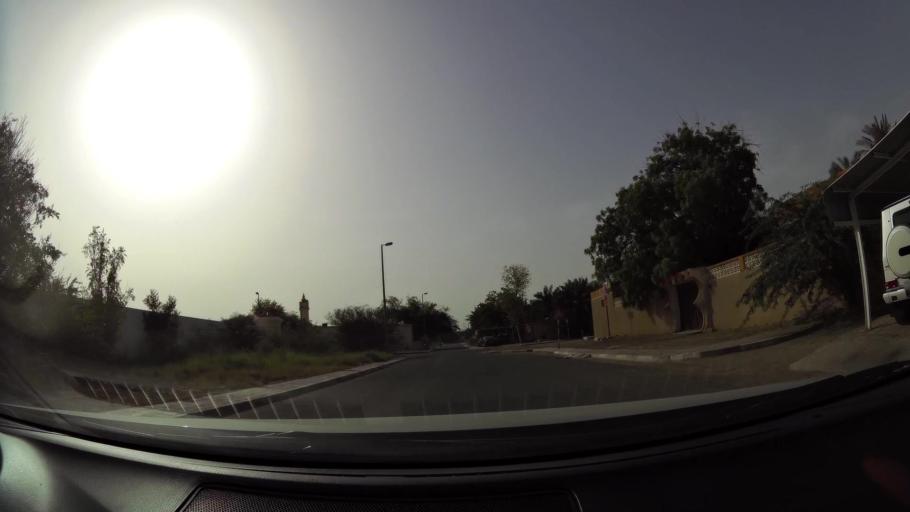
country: AE
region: Abu Dhabi
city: Al Ain
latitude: 24.1378
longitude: 55.6910
